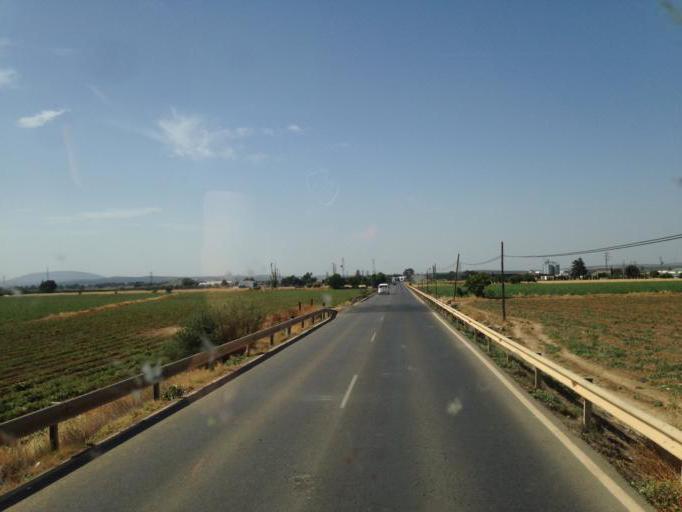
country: ES
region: Andalusia
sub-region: Provincia de Malaga
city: Antequera
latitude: 37.0456
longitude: -4.5621
